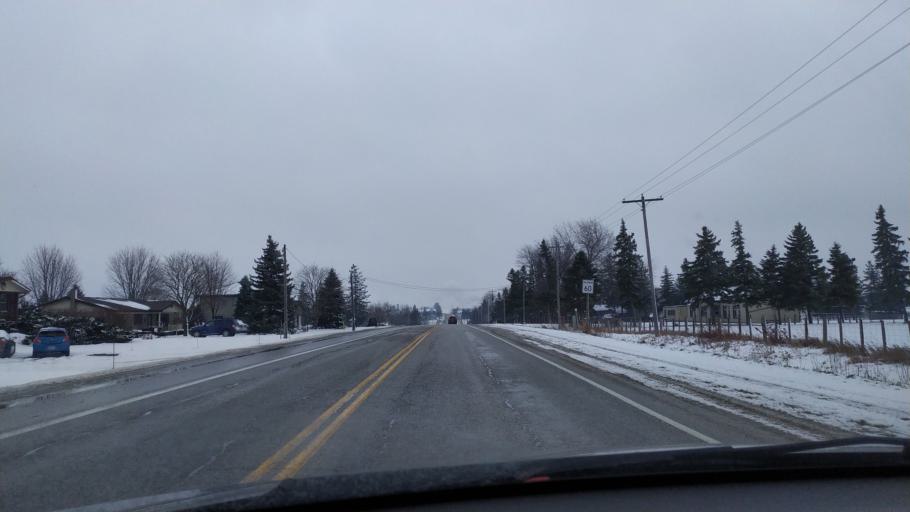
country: CA
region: Ontario
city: Waterloo
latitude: 43.5977
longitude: -80.6295
